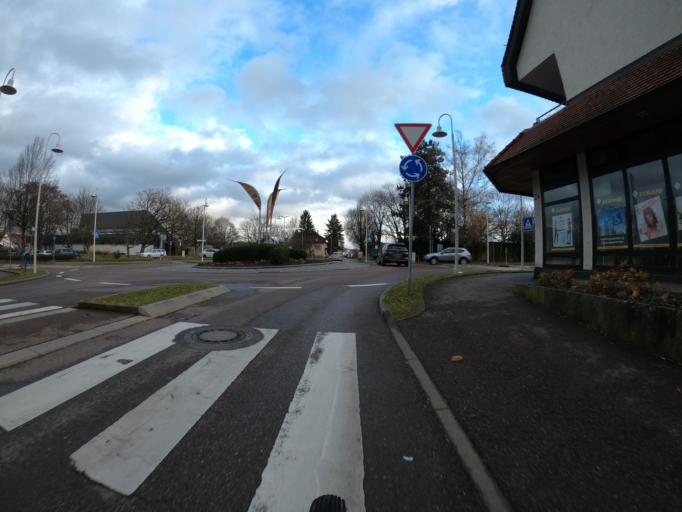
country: DE
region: Baden-Wuerttemberg
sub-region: Regierungsbezirk Stuttgart
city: Eislingen
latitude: 48.6926
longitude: 9.7050
